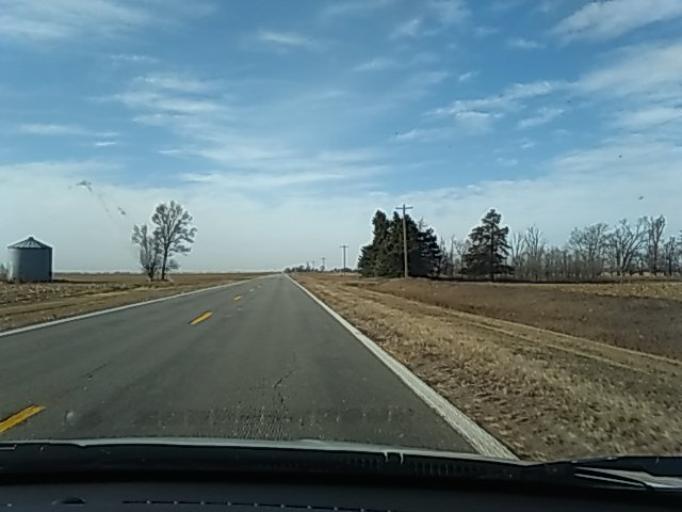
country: US
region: Nebraska
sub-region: Clay County
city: Clay Center
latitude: 40.4233
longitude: -98.0413
